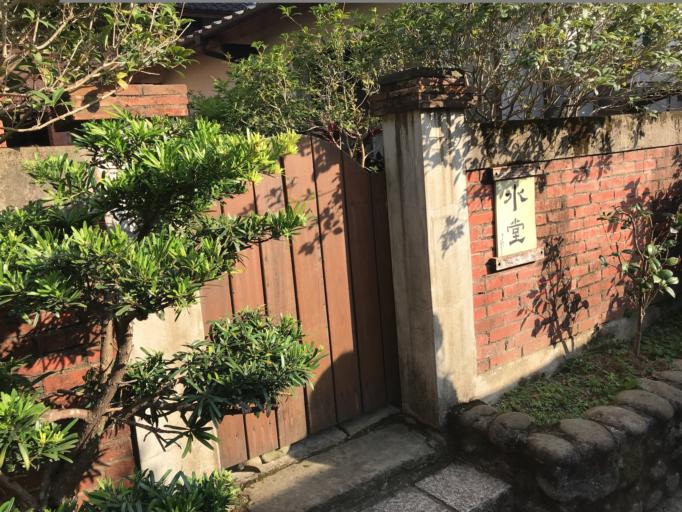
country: TW
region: Taiwan
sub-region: Hsinchu
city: Hsinchu
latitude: 24.6994
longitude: 121.0583
